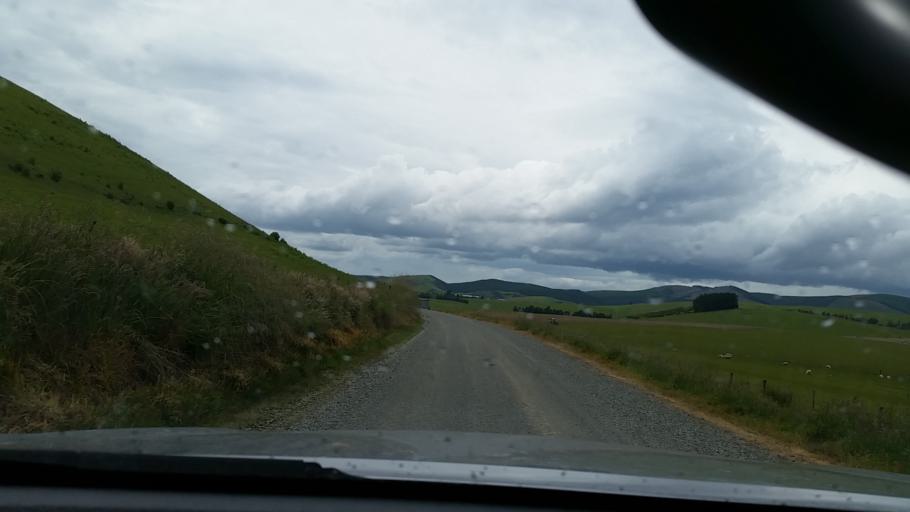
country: NZ
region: Southland
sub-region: Southland District
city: Winton
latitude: -45.8705
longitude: 168.1403
